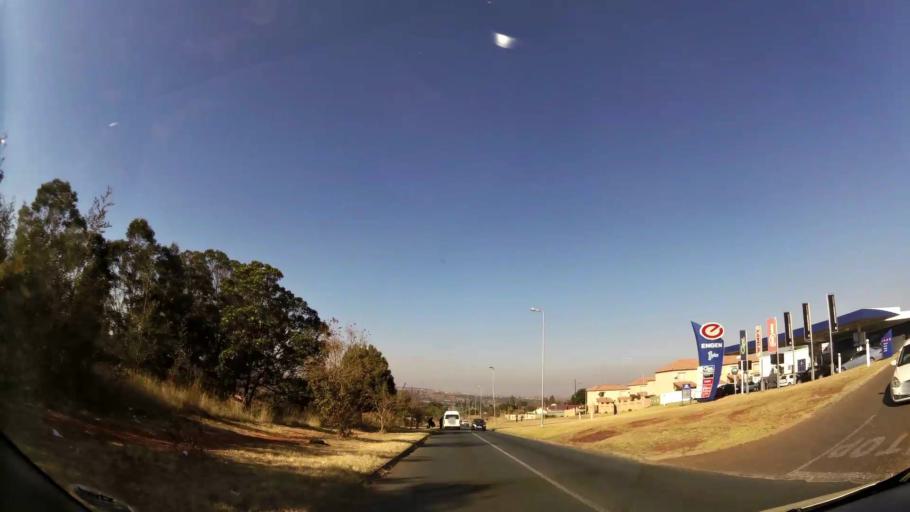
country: ZA
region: Gauteng
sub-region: City of Johannesburg Metropolitan Municipality
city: Roodepoort
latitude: -26.1565
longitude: 27.8328
